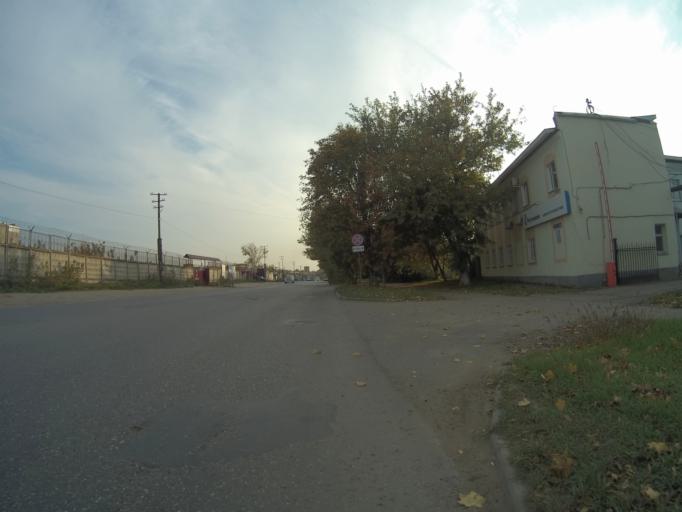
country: RU
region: Vladimir
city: Vladimir
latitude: 56.1576
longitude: 40.3844
